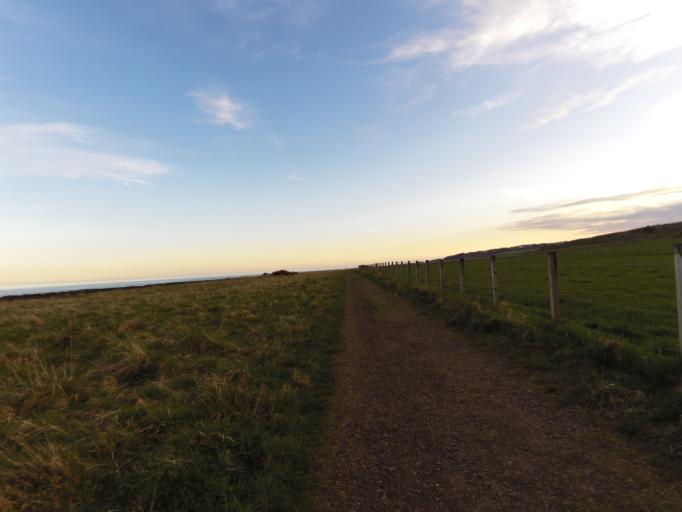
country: GB
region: Scotland
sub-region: Aberdeenshire
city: Inverbervie
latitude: 56.8204
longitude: -2.2956
